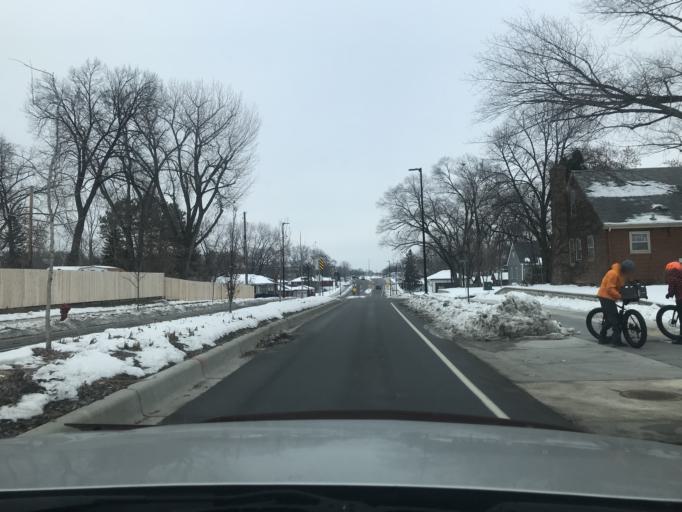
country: US
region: Minnesota
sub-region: Hennepin County
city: Richfield
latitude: 44.8835
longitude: -93.2725
